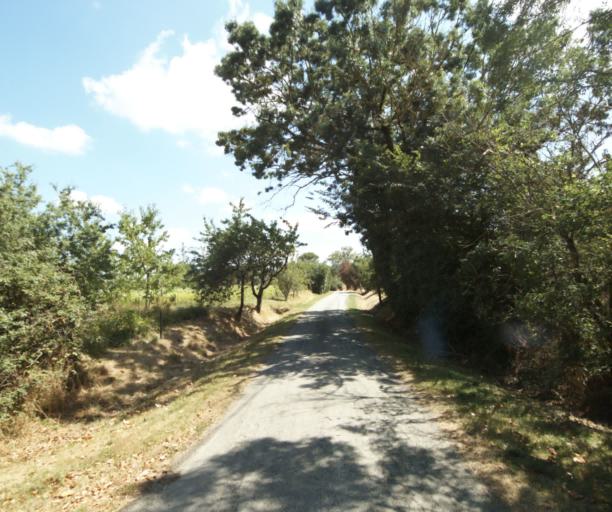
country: FR
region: Midi-Pyrenees
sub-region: Departement de la Haute-Garonne
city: Auriac-sur-Vendinelle
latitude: 43.4665
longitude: 1.7973
